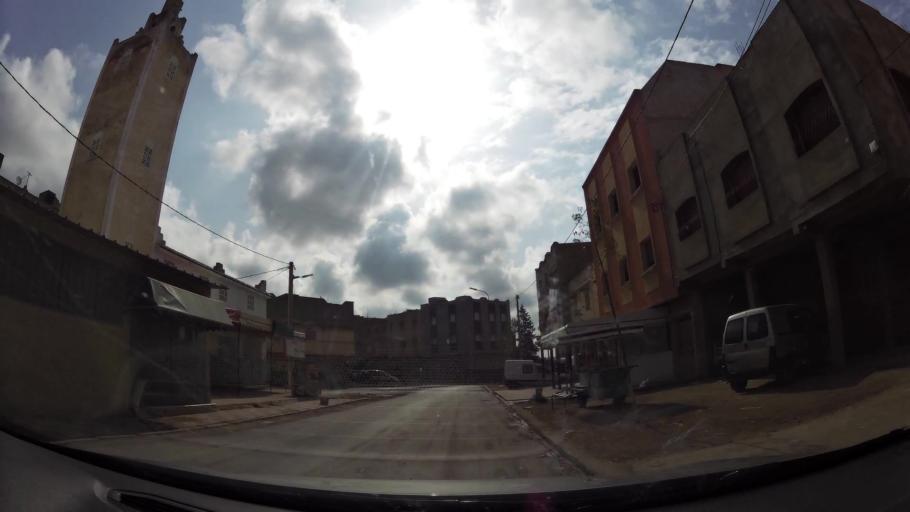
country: MA
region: Rabat-Sale-Zemmour-Zaer
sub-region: Khemisset
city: Tiflet
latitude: 33.8854
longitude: -6.3130
